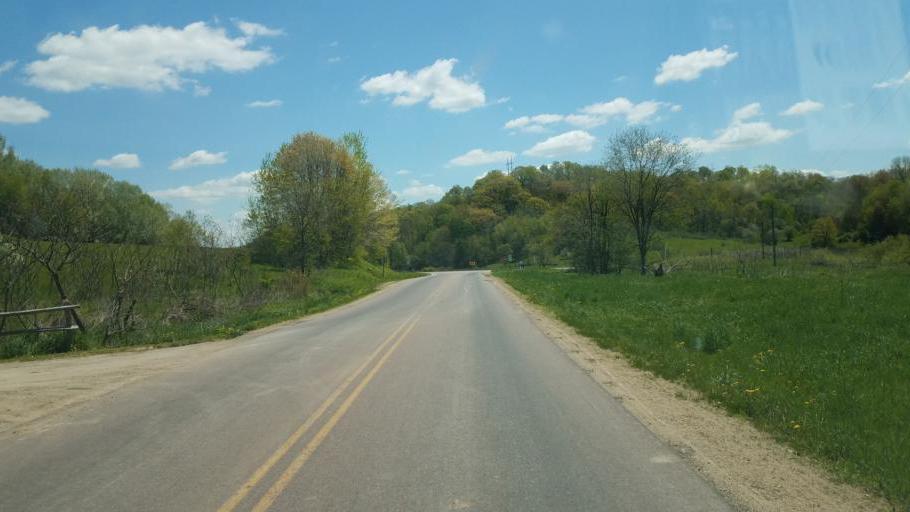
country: US
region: Wisconsin
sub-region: Vernon County
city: Hillsboro
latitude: 43.6453
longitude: -90.4381
